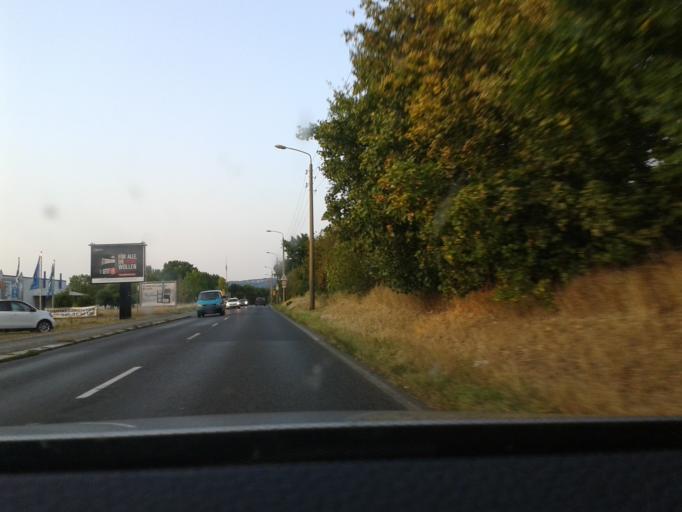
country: DE
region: Saxony
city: Kreischa
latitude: 51.0001
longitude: 13.8013
